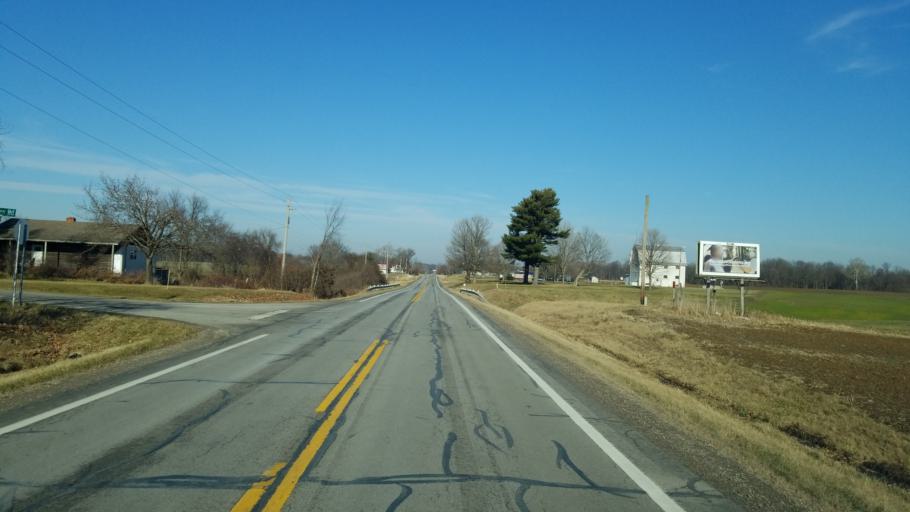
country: US
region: Ohio
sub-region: Huron County
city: Norwalk
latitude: 41.1568
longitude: -82.6500
